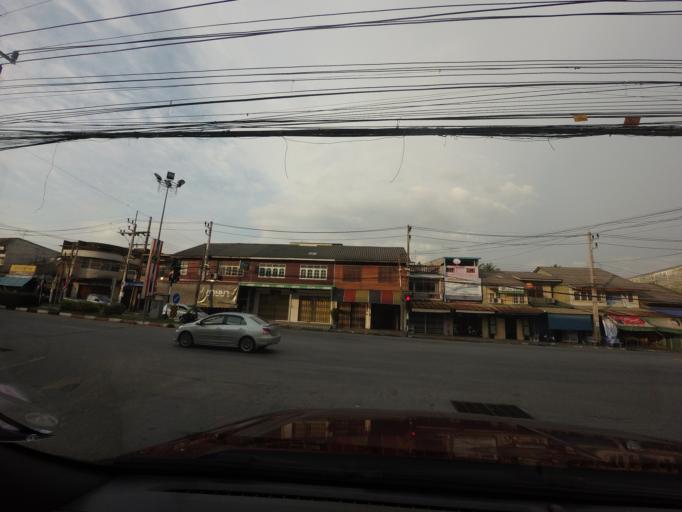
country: TH
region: Pattani
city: Khok Pho
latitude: 6.6788
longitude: 101.1458
